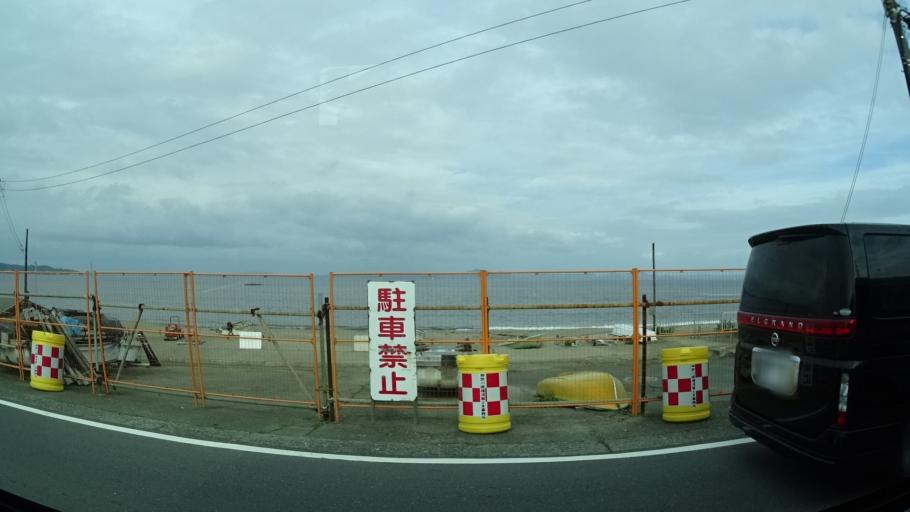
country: JP
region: Kanagawa
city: Miura
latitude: 35.1756
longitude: 139.6543
